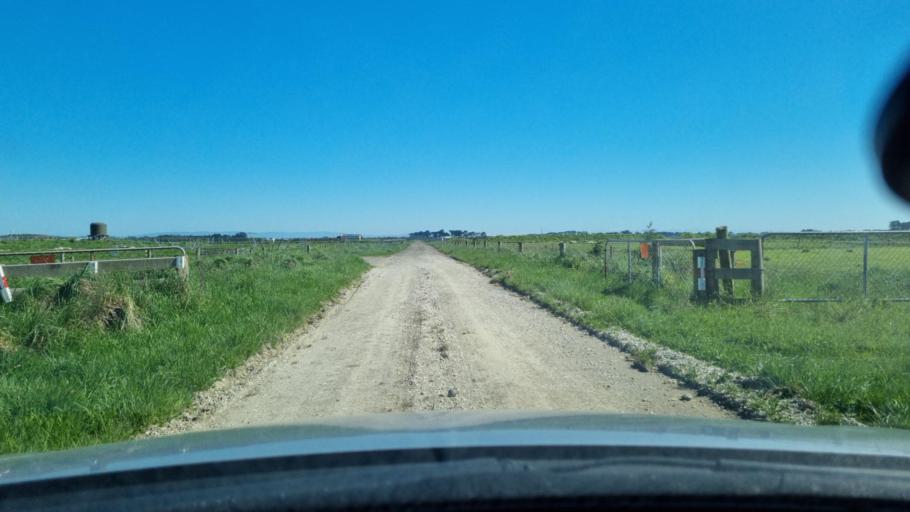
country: NZ
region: Southland
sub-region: Invercargill City
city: Invercargill
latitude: -46.4221
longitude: 168.3122
